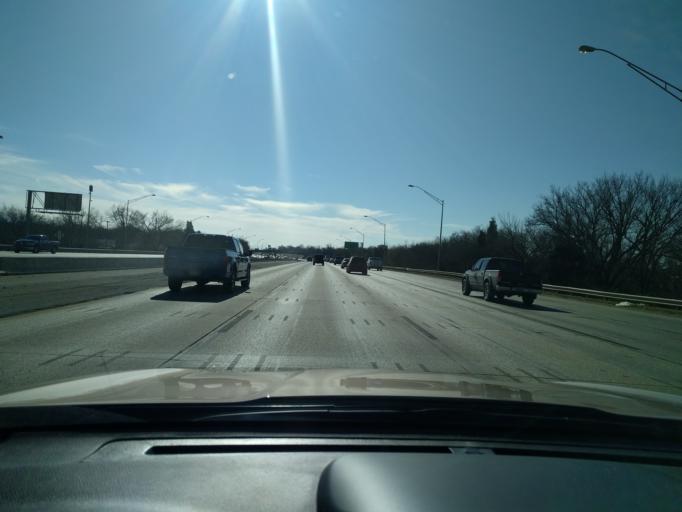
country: US
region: Oklahoma
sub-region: Oklahoma County
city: Warr Acres
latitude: 35.5021
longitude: -97.5778
